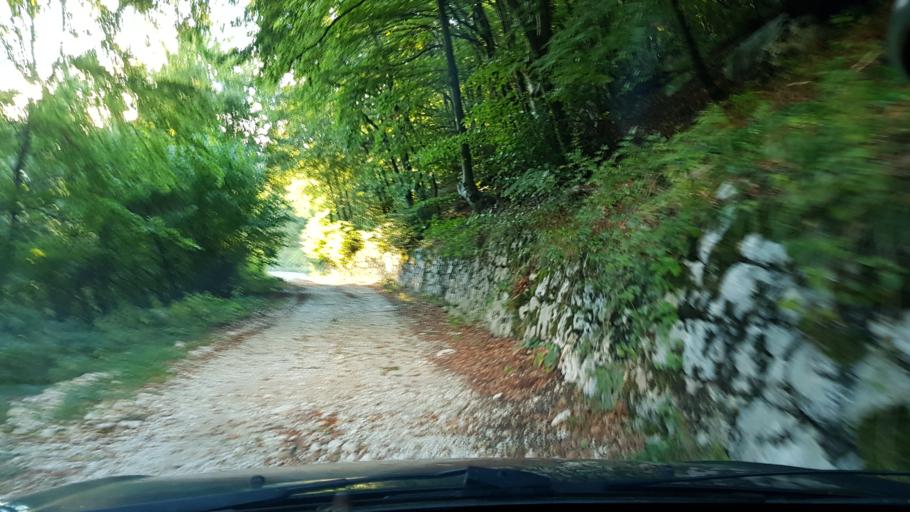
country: SI
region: Kobarid
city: Kobarid
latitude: 46.2772
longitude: 13.6208
